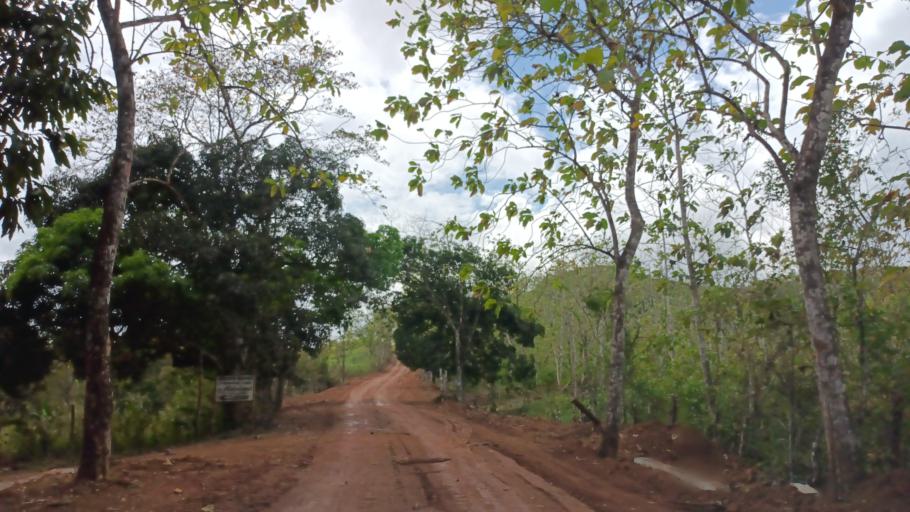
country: PA
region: Panama
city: La Cabima
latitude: 9.1181
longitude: -79.4969
